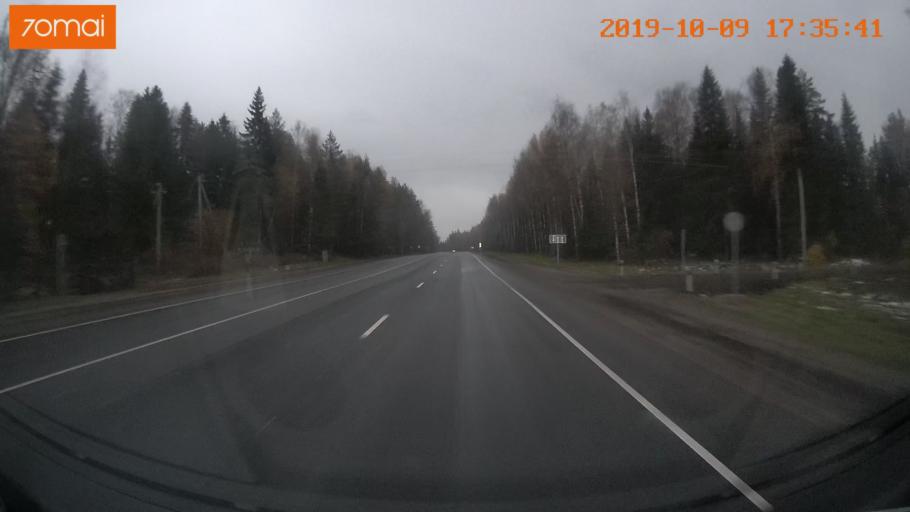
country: RU
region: Ivanovo
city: Bogorodskoye
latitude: 57.0898
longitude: 41.0004
